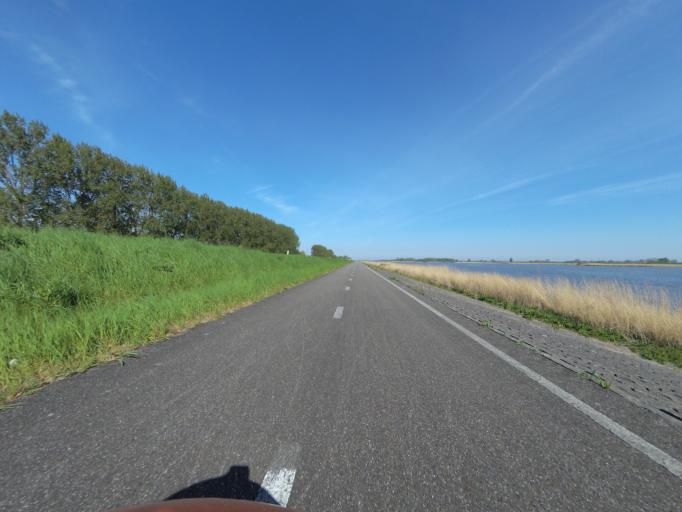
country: NL
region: Overijssel
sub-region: Gemeente Kampen
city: Kampen
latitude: 52.5535
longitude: 5.8484
